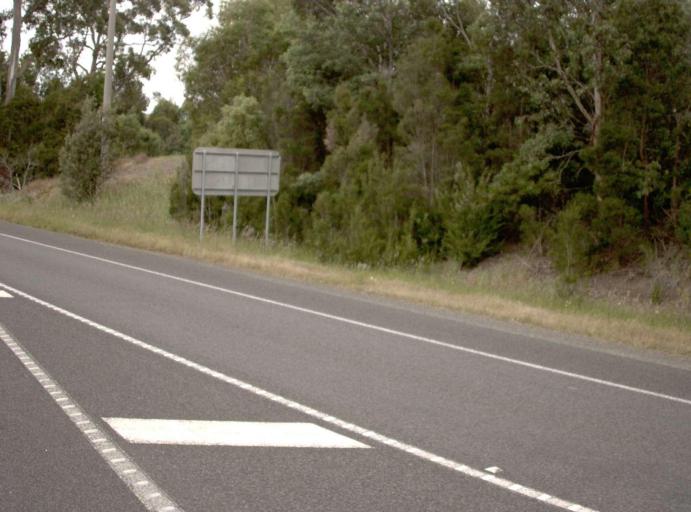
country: AU
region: Victoria
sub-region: Bass Coast
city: North Wonthaggi
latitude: -38.3657
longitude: 145.6991
